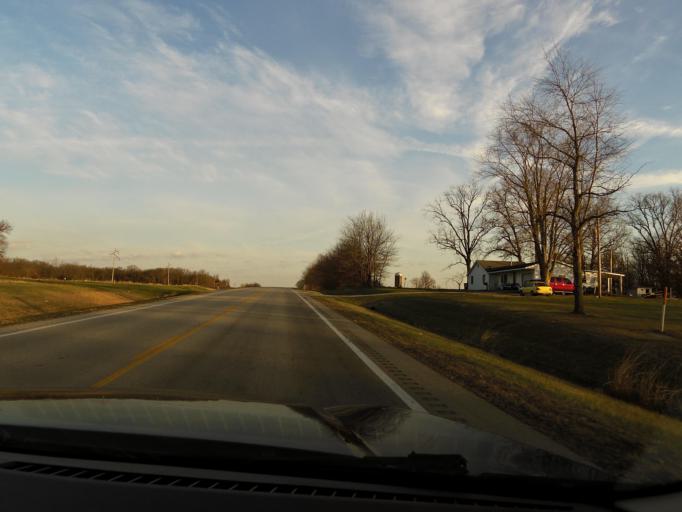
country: US
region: Illinois
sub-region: Fayette County
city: Vandalia
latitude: 38.8555
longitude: -89.0879
